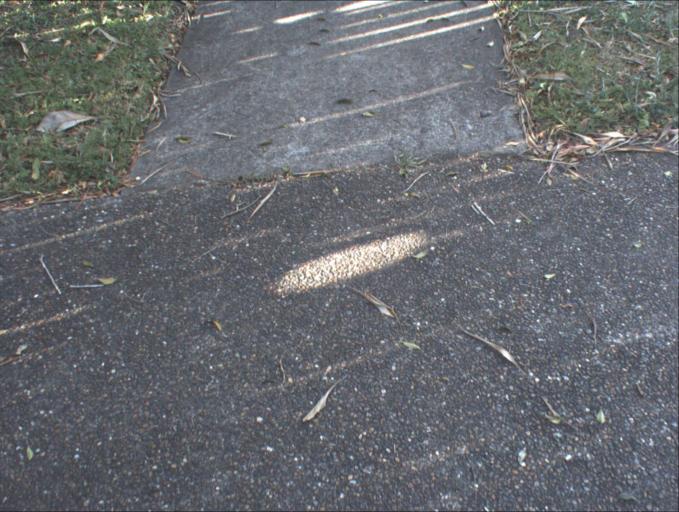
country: AU
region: Queensland
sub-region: Logan
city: Slacks Creek
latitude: -27.6565
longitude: 153.1613
